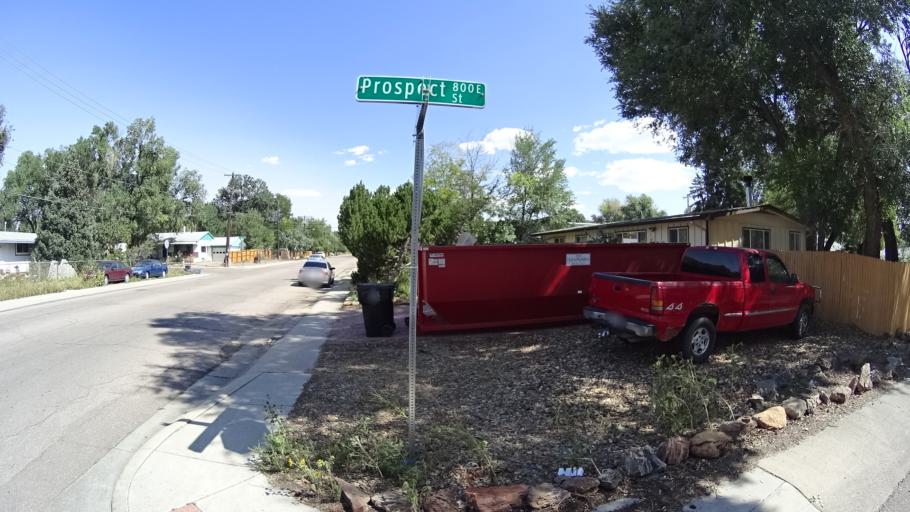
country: US
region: Colorado
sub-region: El Paso County
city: Colorado Springs
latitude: 38.8786
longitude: -104.8110
